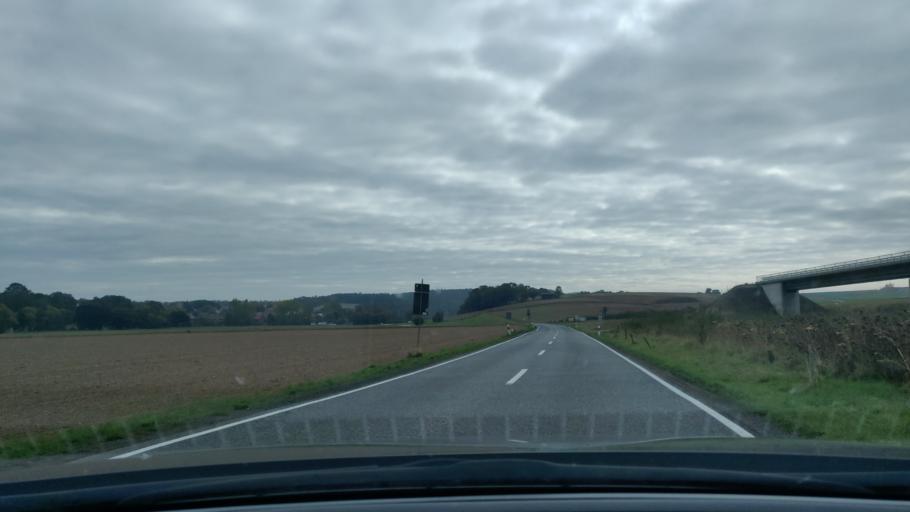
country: DE
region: Hesse
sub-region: Regierungsbezirk Kassel
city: Neuental
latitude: 51.0023
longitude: 9.2014
